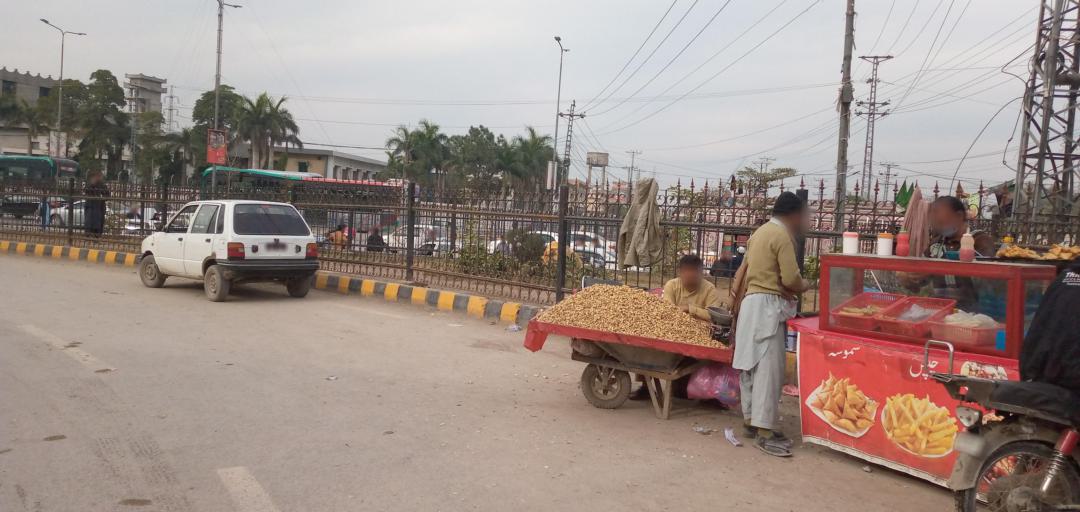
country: PK
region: Khyber Pakhtunkhwa
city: Peshawar
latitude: 33.9974
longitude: 71.4695
